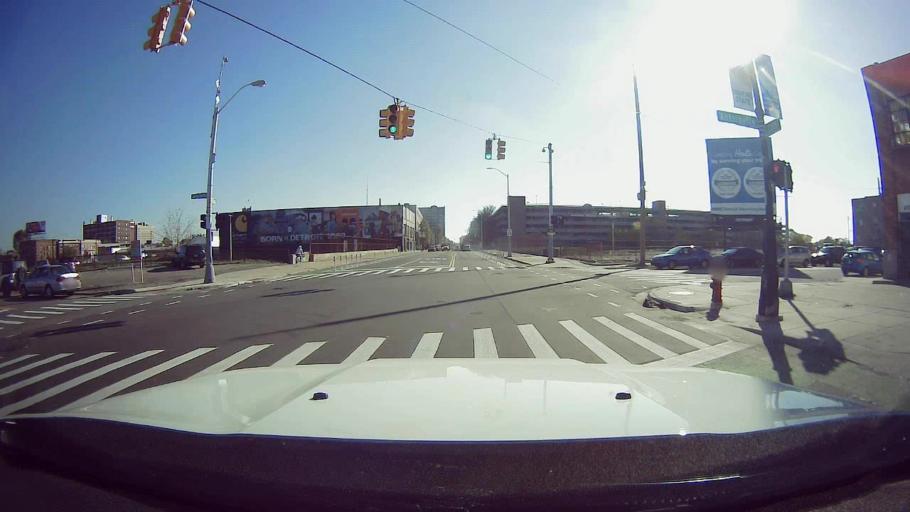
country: US
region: Michigan
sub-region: Wayne County
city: Hamtramck
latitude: 42.3634
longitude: -83.0708
